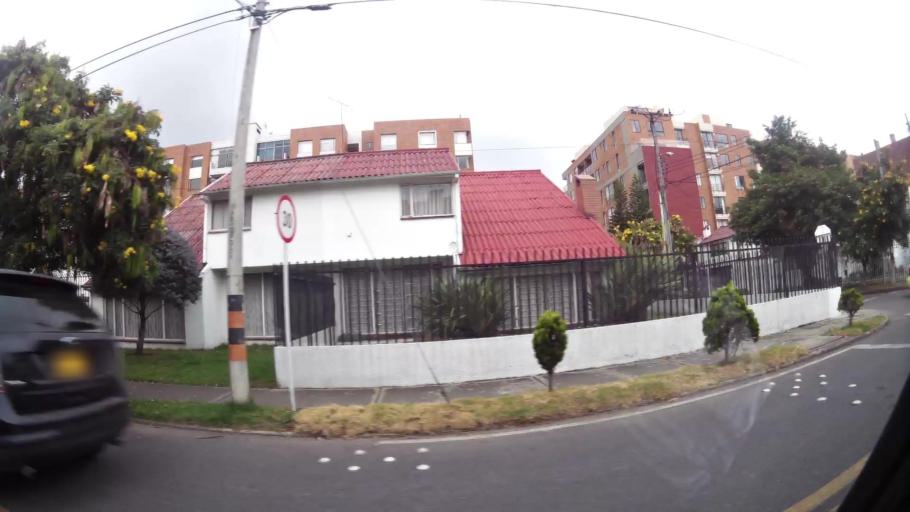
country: CO
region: Bogota D.C.
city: Barrio San Luis
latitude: 4.7185
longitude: -74.0430
